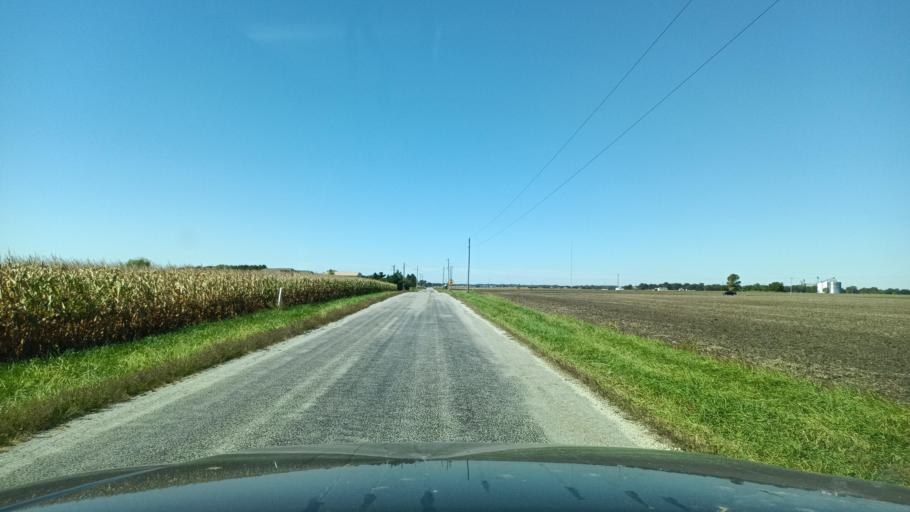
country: US
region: Illinois
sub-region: Champaign County
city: Mahomet
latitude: 40.0987
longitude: -88.4037
